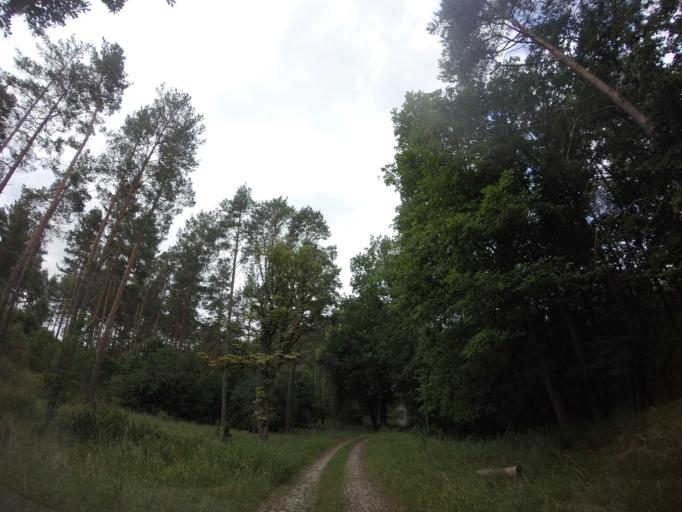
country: PL
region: Lubusz
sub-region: Powiat strzelecko-drezdenecki
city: Strzelce Krajenskie
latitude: 52.9224
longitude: 15.6010
